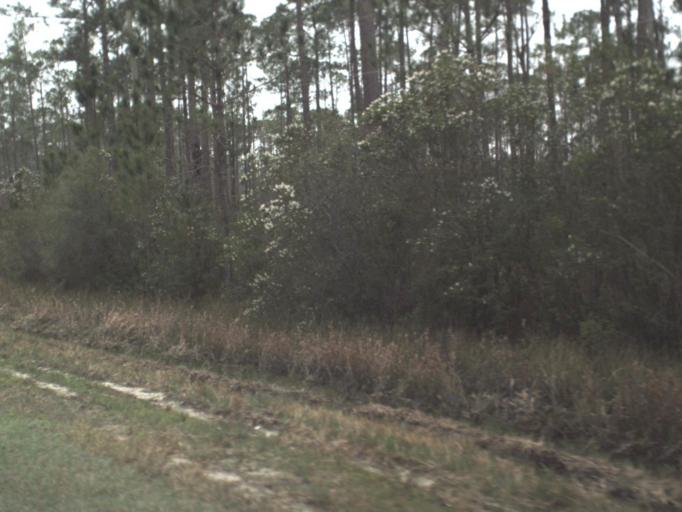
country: US
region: Florida
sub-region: Liberty County
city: Bristol
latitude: 30.2961
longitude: -84.8330
